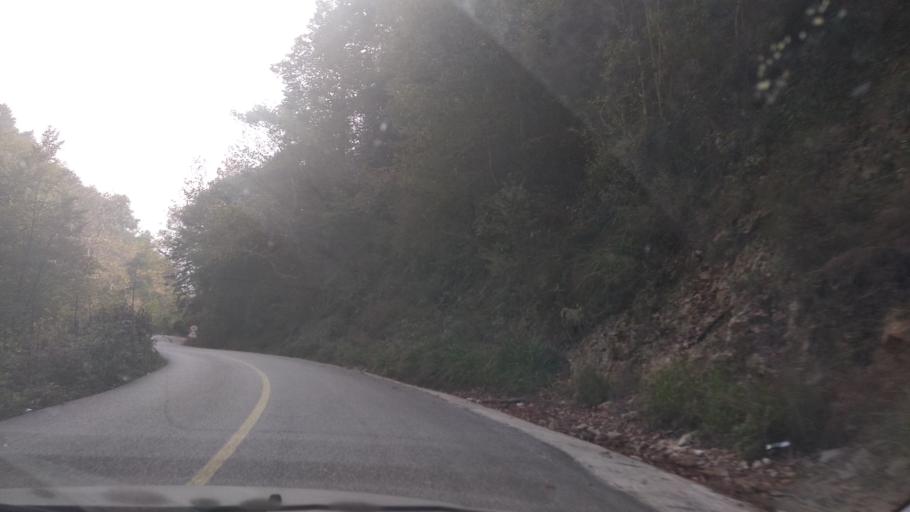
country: TR
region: Duzce
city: Kaynasli
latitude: 40.7220
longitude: 31.2622
